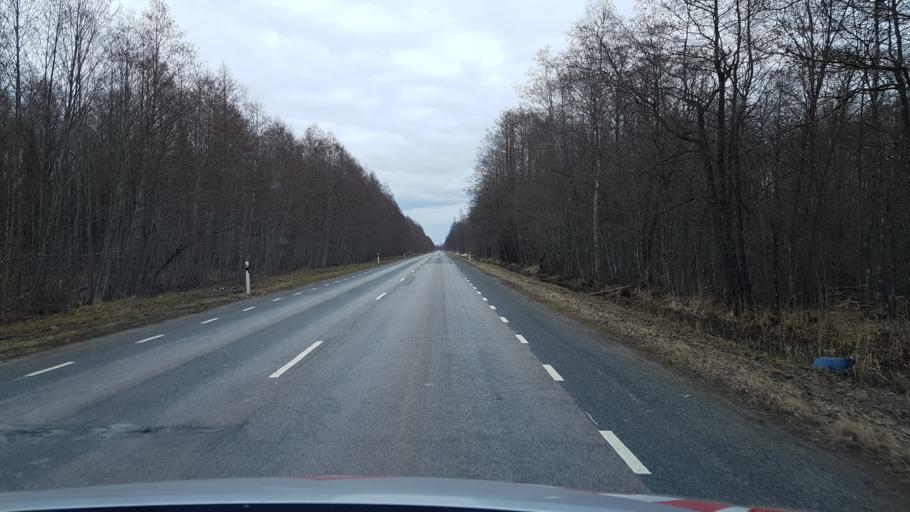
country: EE
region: Ida-Virumaa
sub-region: Narva-Joesuu linn
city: Narva-Joesuu
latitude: 59.3516
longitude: 28.0558
